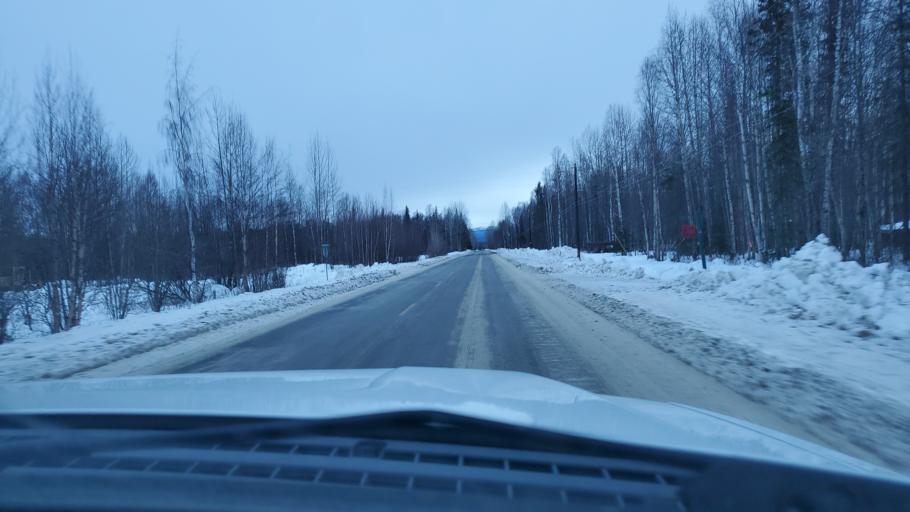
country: US
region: Alaska
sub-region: Matanuska-Susitna Borough
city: Y
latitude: 62.3163
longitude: -150.2554
